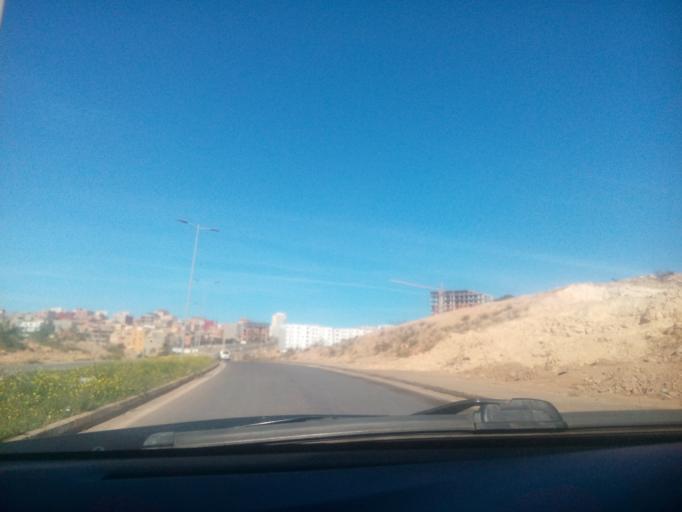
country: DZ
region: Oran
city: Bir el Djir
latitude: 35.7407
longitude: -0.5466
